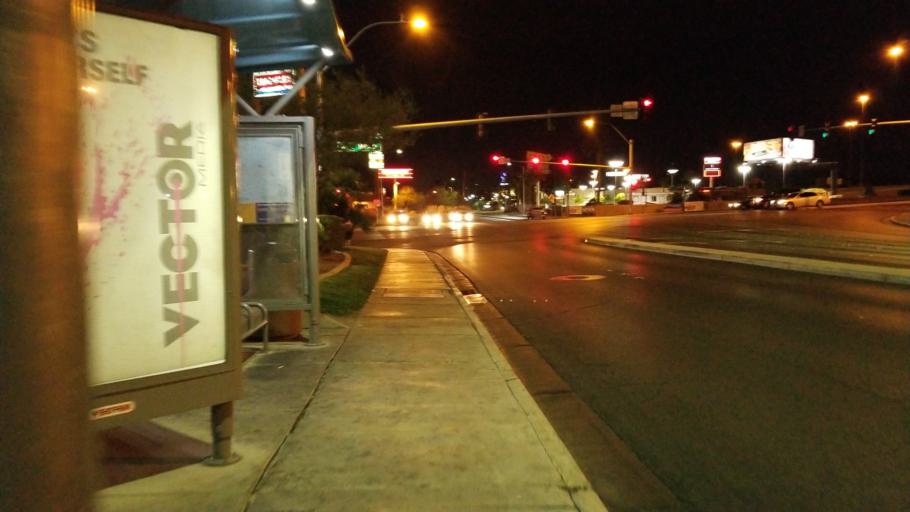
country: US
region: Nevada
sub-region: Clark County
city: Spring Valley
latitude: 36.1965
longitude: -115.2418
